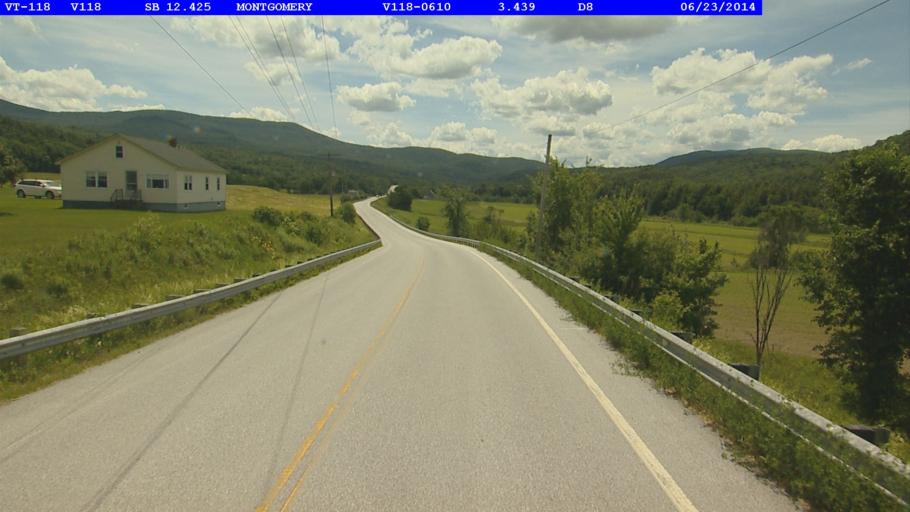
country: US
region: Vermont
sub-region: Franklin County
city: Richford
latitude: 44.8472
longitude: -72.6106
